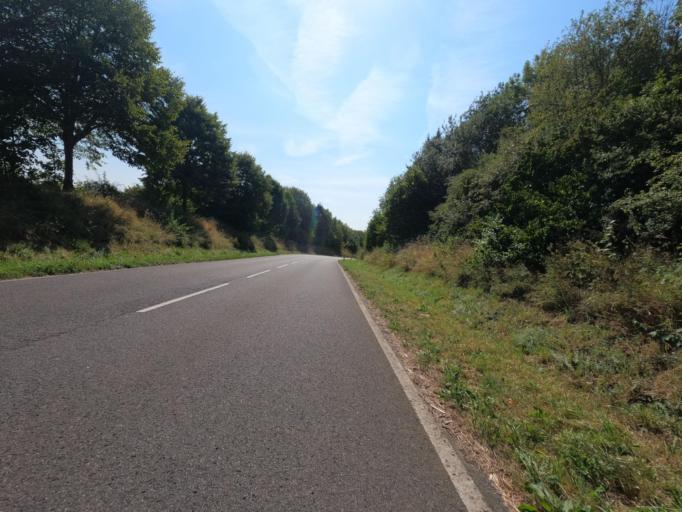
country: DE
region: North Rhine-Westphalia
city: Julich
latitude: 50.9785
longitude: 6.3461
